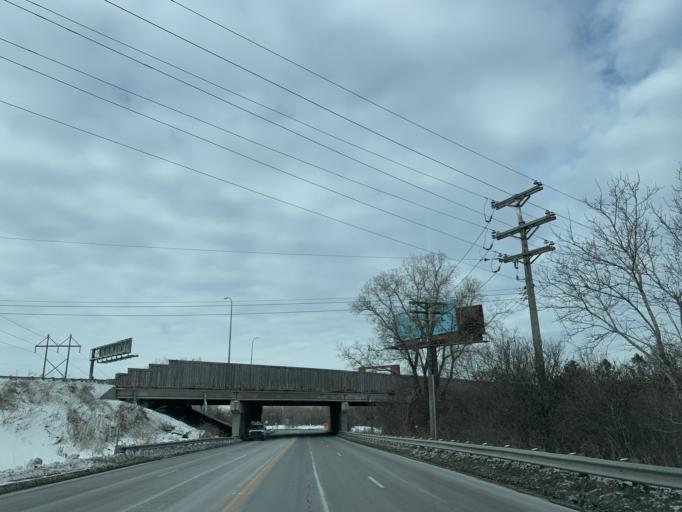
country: US
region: Minnesota
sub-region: Ramsey County
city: Lauderdale
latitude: 44.9766
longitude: -93.2016
